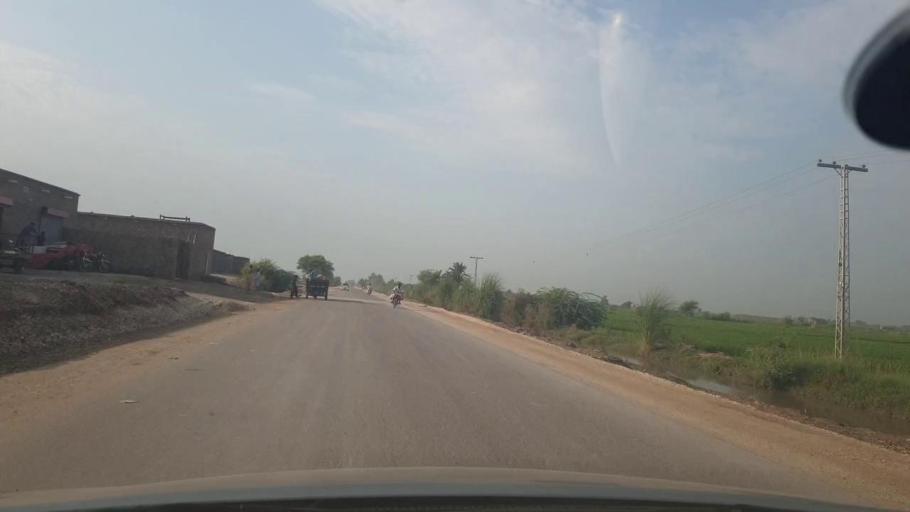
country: PK
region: Sindh
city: Jacobabad
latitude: 28.2120
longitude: 68.3685
